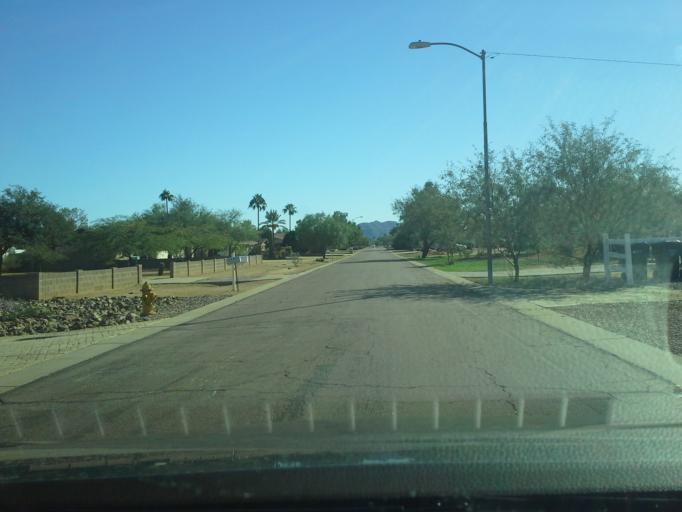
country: US
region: Arizona
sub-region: Maricopa County
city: Paradise Valley
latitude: 33.6373
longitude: -111.9920
